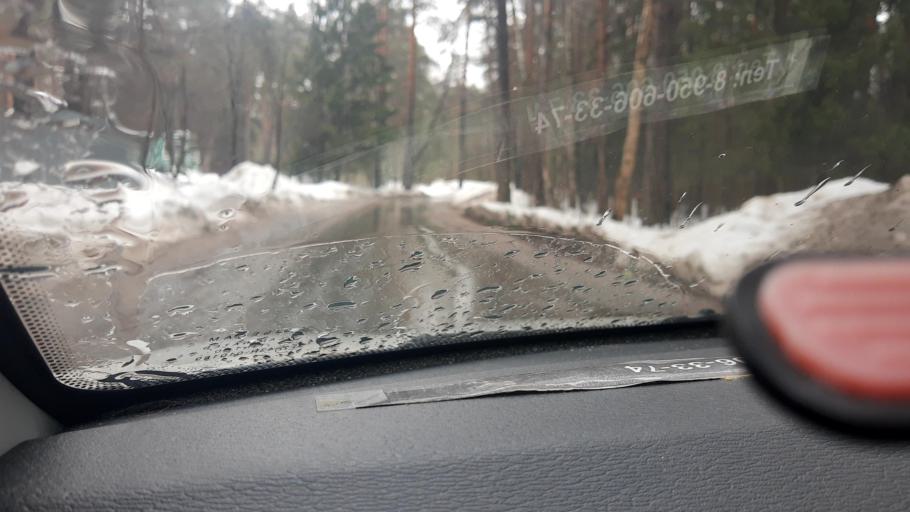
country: RU
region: Nizjnij Novgorod
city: Afonino
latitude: 56.1644
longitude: 44.0912
